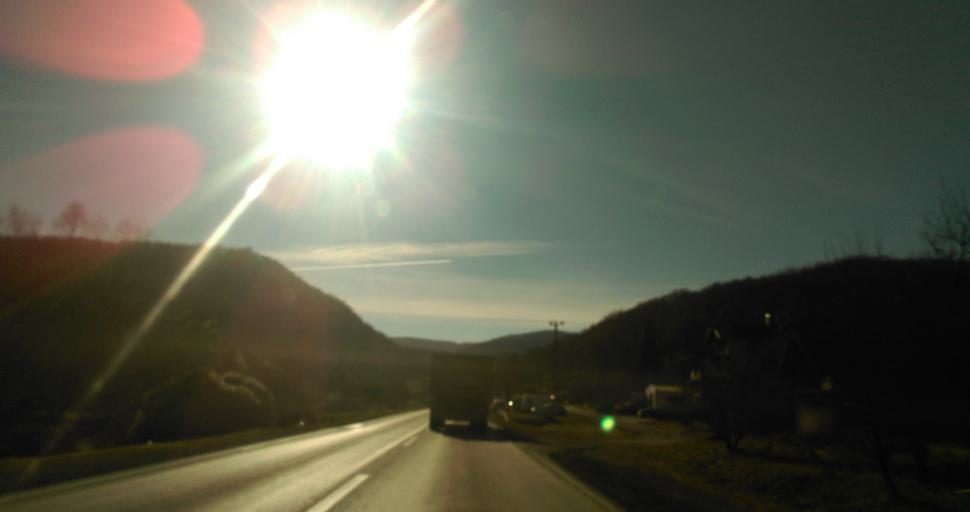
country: RS
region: Autonomna Pokrajina Vojvodina
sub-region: Juznobacki Okrug
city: Novi Sad
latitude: 45.1892
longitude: 19.8404
